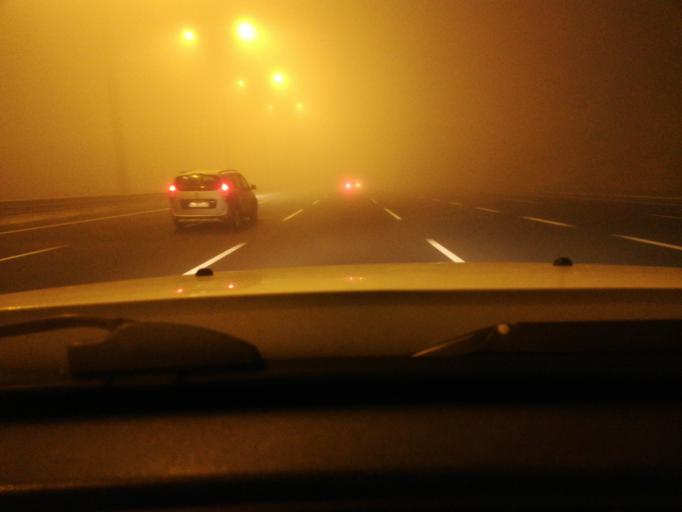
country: TR
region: Istanbul
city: Sultanbeyli
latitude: 40.9790
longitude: 29.3278
